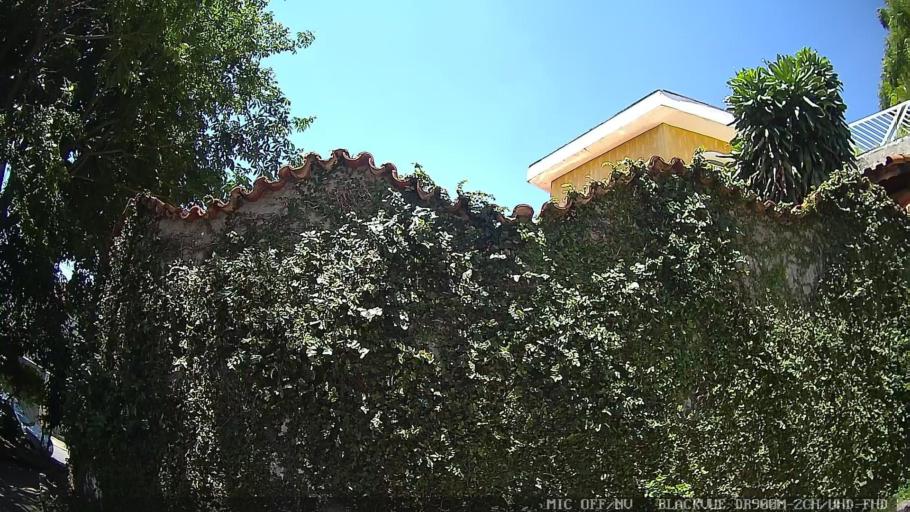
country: BR
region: Sao Paulo
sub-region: Sao Caetano Do Sul
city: Sao Caetano do Sul
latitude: -23.5925
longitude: -46.5357
